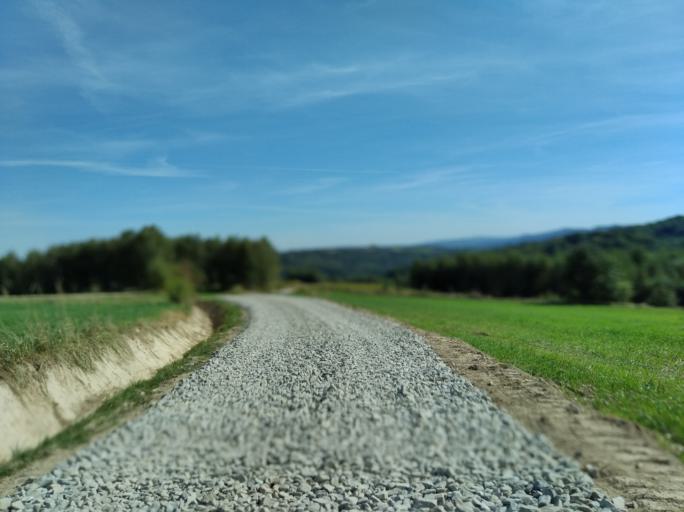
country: PL
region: Subcarpathian Voivodeship
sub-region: Powiat strzyzowski
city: Wisniowa
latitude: 49.9000
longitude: 21.6247
